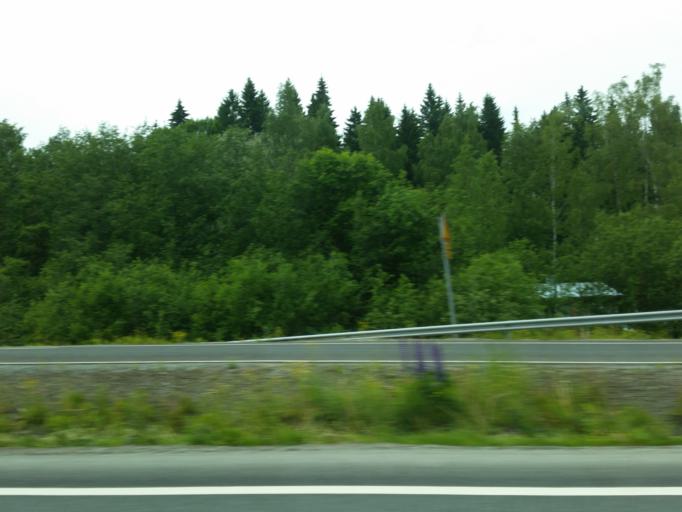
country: FI
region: Northern Savo
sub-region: Kuopio
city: Kuopio
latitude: 62.9613
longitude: 27.6929
